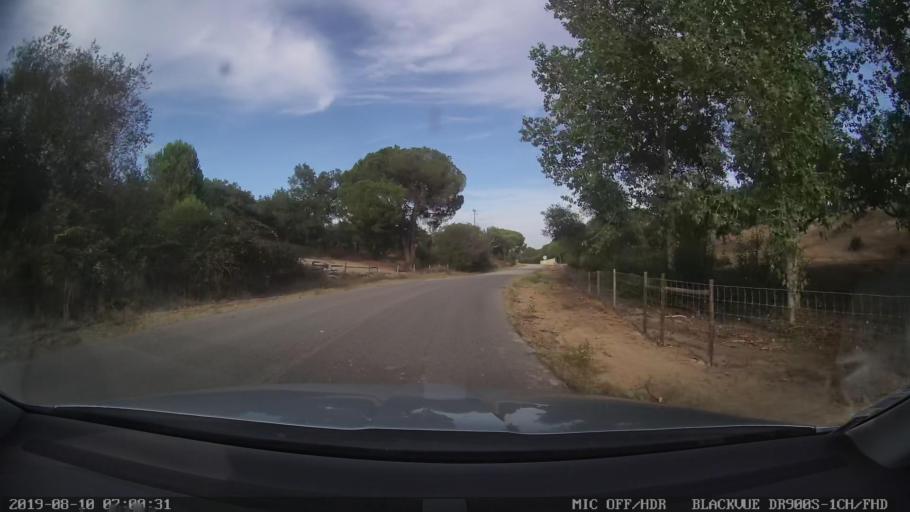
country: PT
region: Santarem
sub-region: Benavente
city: Poceirao
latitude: 38.8478
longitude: -8.7020
